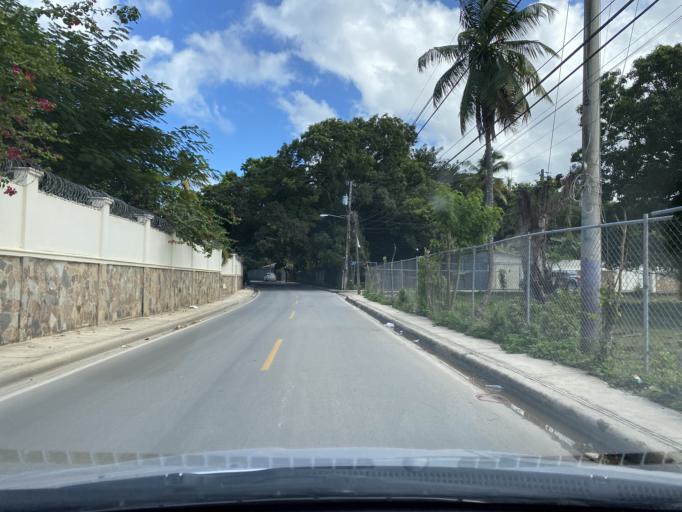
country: DO
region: Samana
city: Las Terrenas
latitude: 19.3076
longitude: -69.5503
